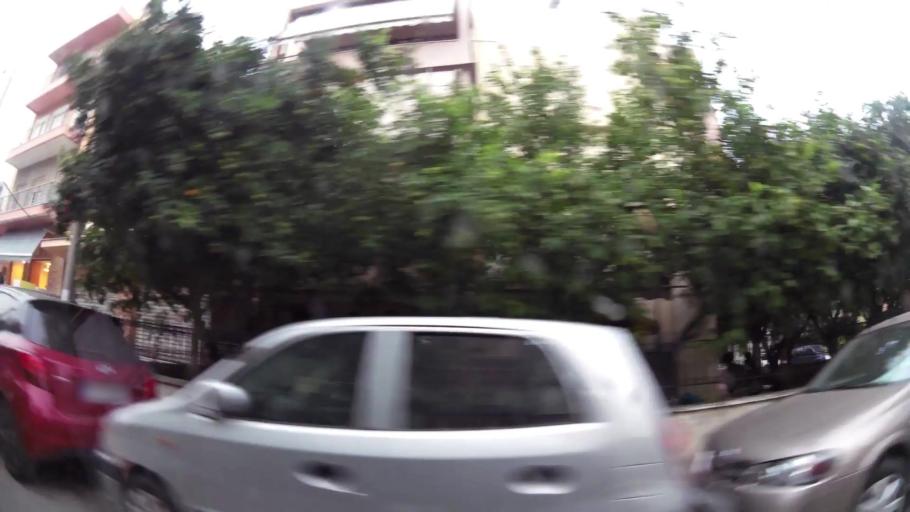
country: GR
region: Attica
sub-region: Nomos Piraios
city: Agios Ioannis Rentis
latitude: 37.9583
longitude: 23.6729
